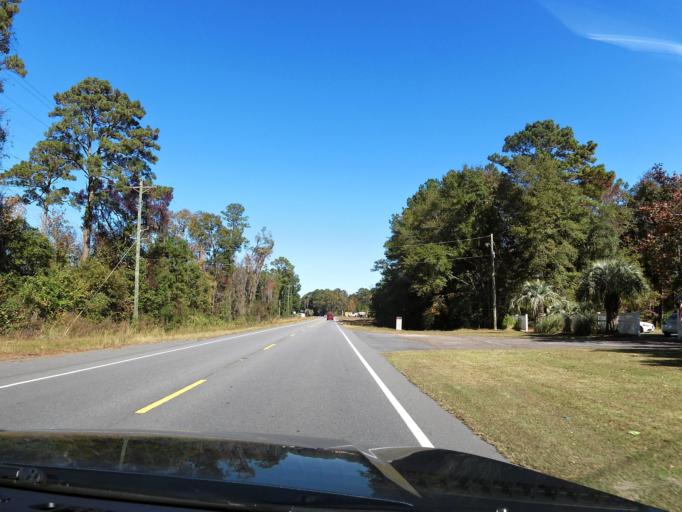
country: US
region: Georgia
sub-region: Liberty County
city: Midway
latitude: 31.8550
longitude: -81.4030
